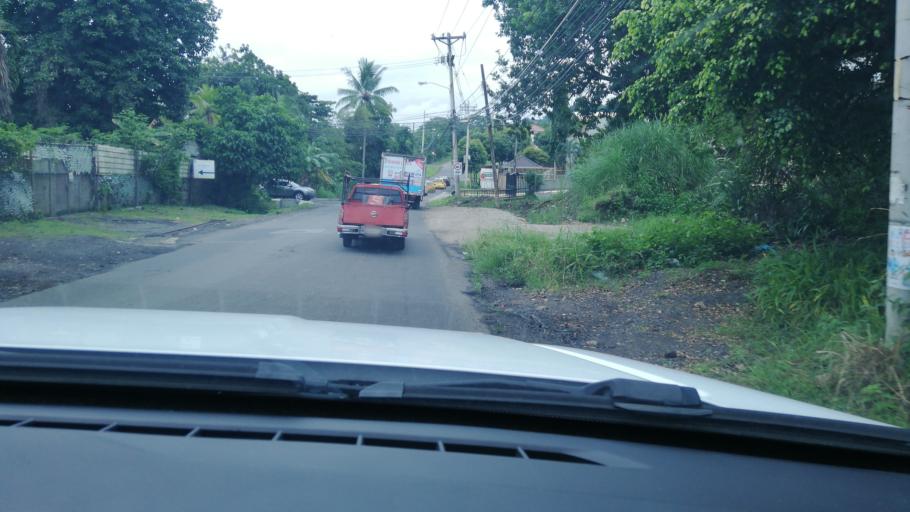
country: PA
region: Panama
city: Las Cumbres
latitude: 9.0756
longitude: -79.5211
